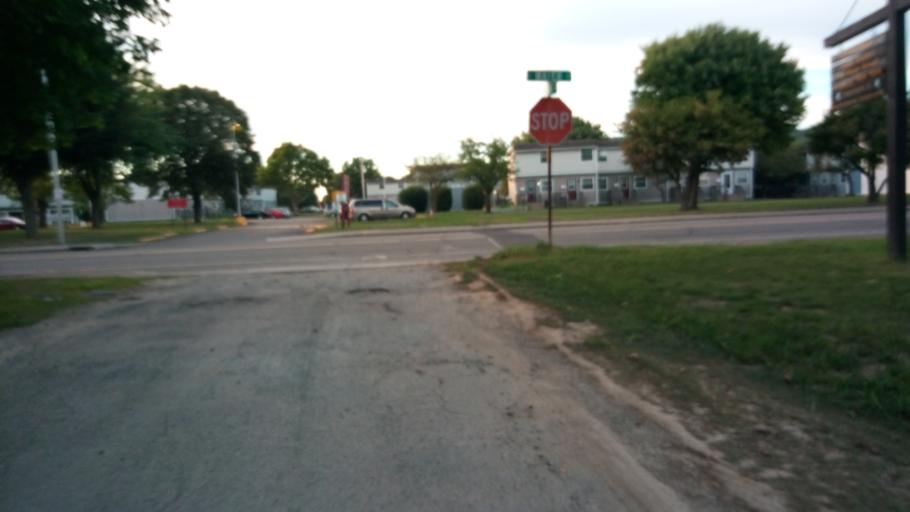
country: US
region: New York
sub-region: Chemung County
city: Elmira
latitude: 42.0892
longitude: -76.7913
